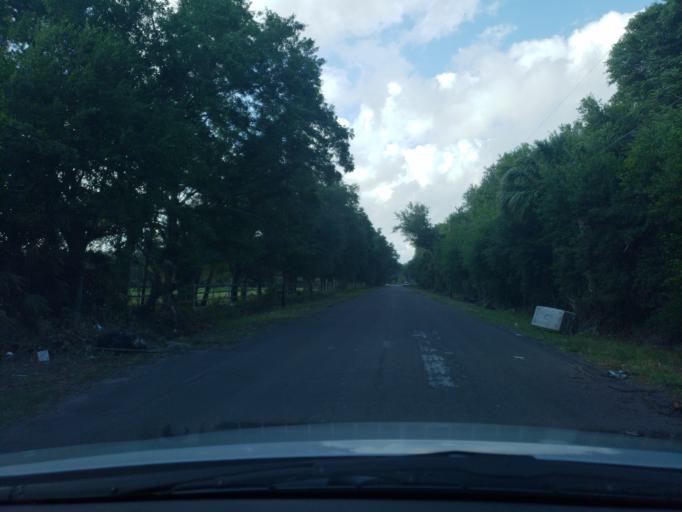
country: US
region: Florida
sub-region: Hillsborough County
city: Palm River-Clair Mel
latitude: 27.9123
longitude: -82.3932
